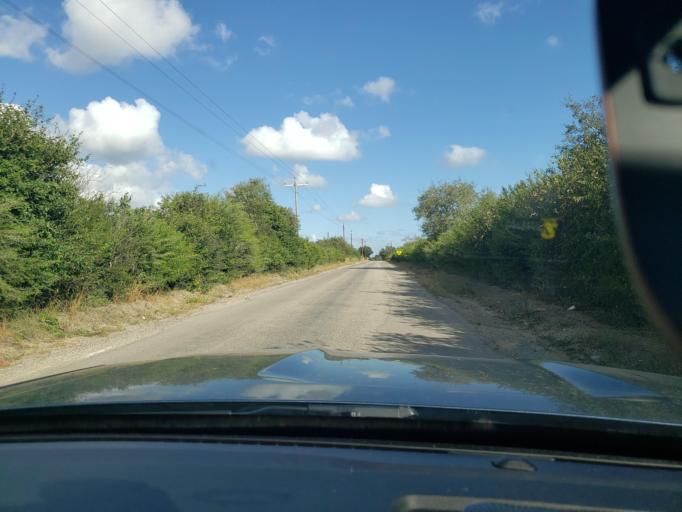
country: US
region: Texas
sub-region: Bee County
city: Beeville
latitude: 28.4567
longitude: -97.7182
